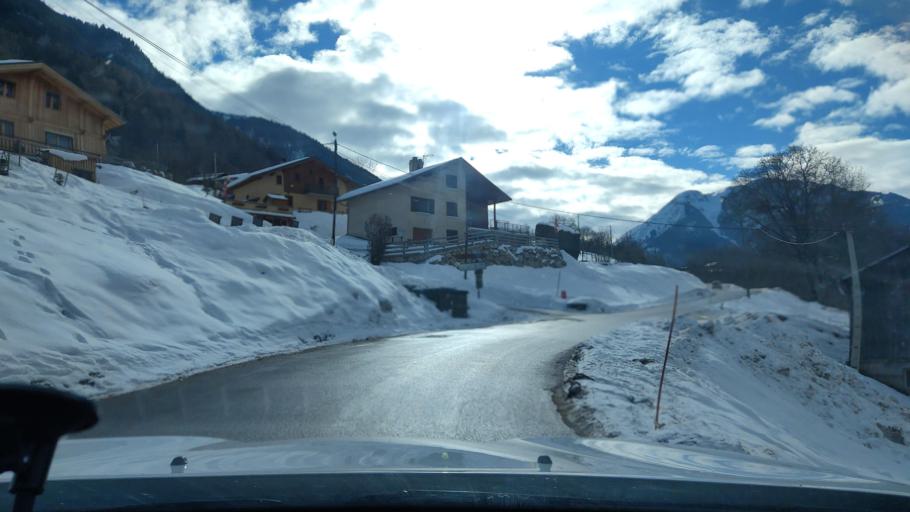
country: FR
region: Rhone-Alpes
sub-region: Departement de la Savoie
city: Salins-les-Thermes
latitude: 45.4401
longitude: 6.5047
